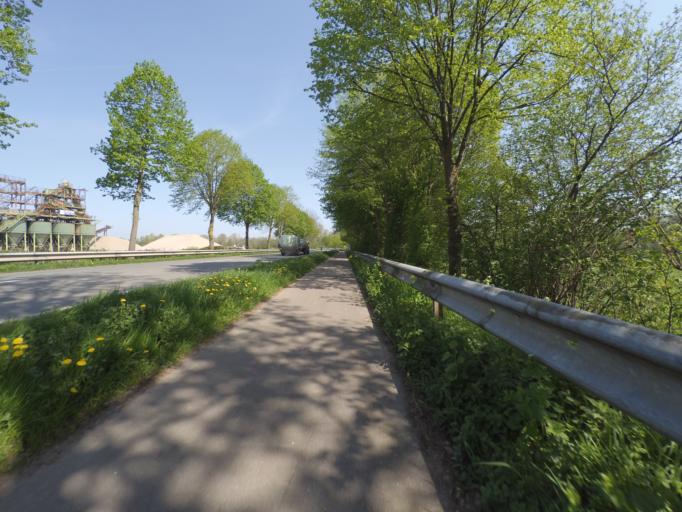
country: DE
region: North Rhine-Westphalia
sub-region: Regierungsbezirk Dusseldorf
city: Mehrhoog
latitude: 51.7152
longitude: 6.5109
